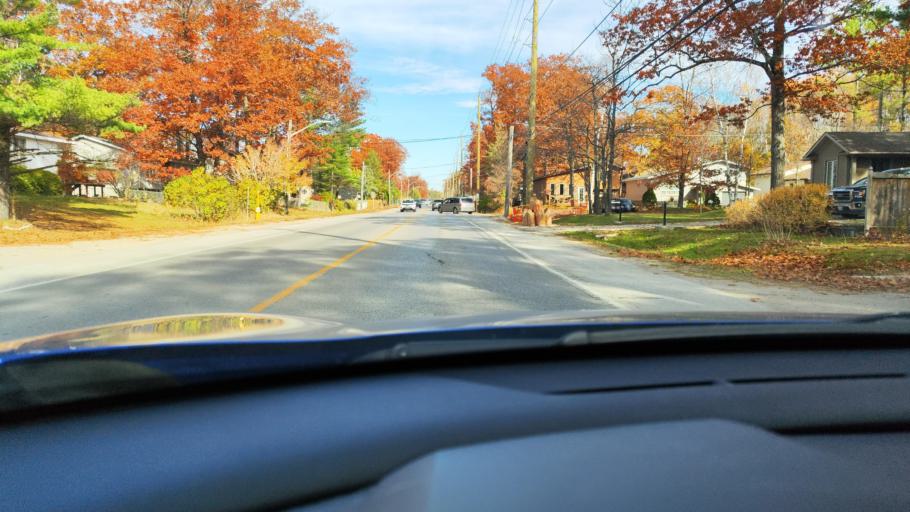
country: CA
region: Ontario
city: Wasaga Beach
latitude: 44.5044
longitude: -80.0329
